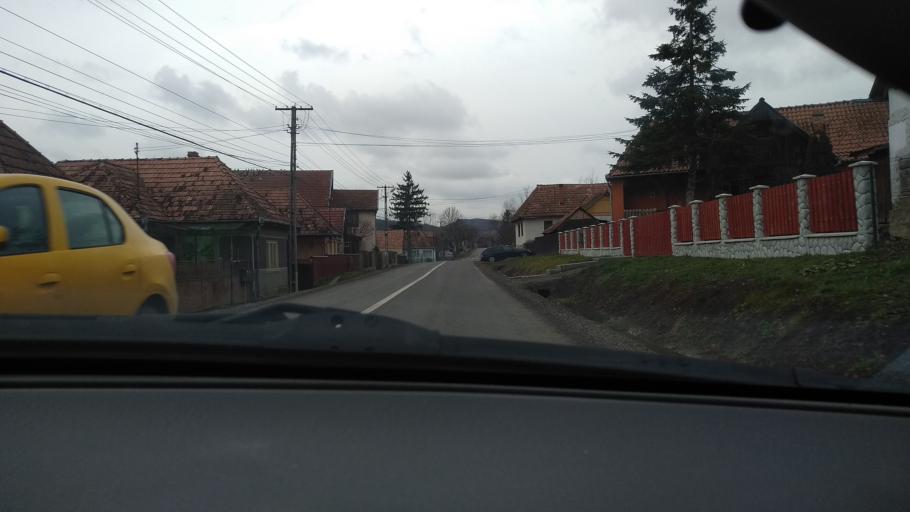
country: RO
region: Mures
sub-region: Comuna Galesti
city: Galesti
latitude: 46.5319
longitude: 24.7673
